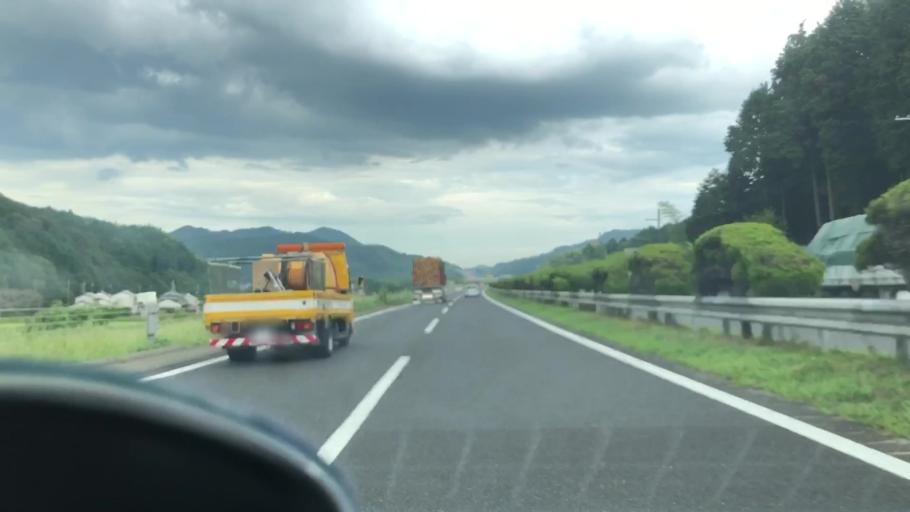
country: JP
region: Hyogo
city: Yamazakicho-nakabirose
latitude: 34.9711
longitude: 134.6653
